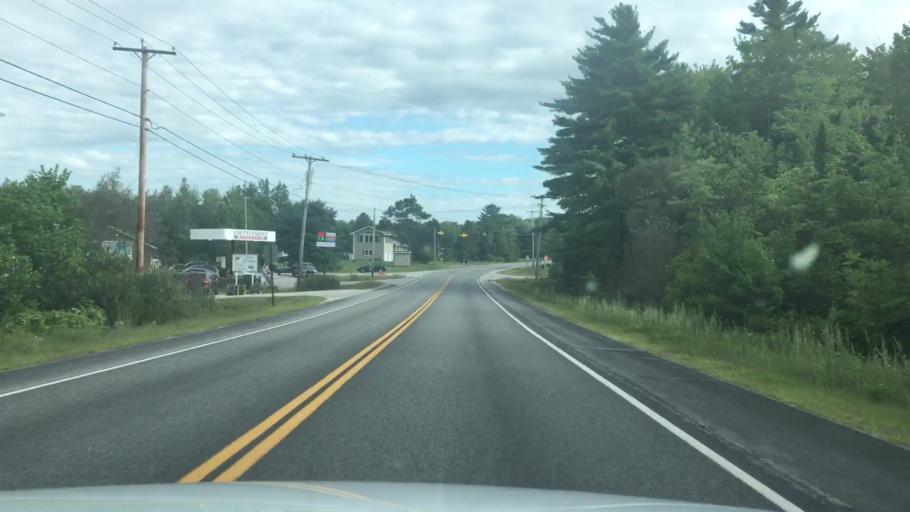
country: US
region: Maine
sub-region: Androscoggin County
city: Lisbon
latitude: 44.0704
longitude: -70.0826
